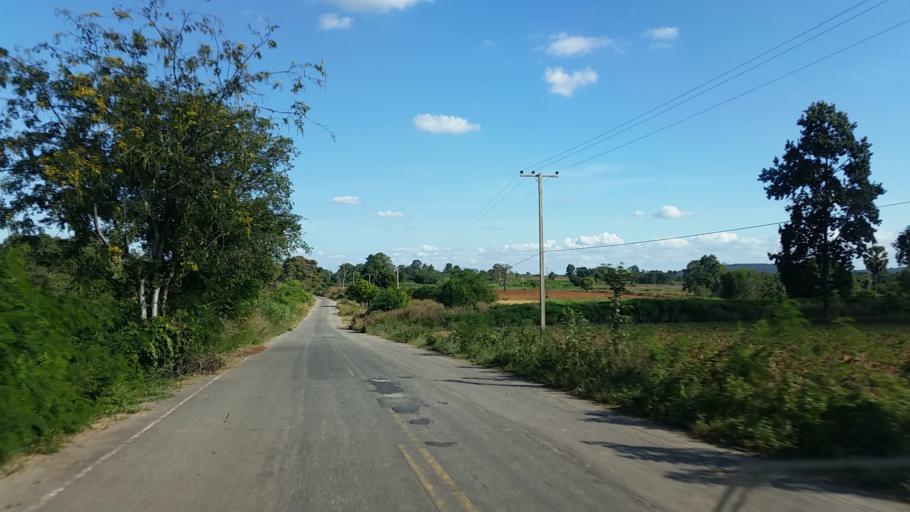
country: TH
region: Chaiyaphum
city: Thep Sathit
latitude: 15.5480
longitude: 101.4538
